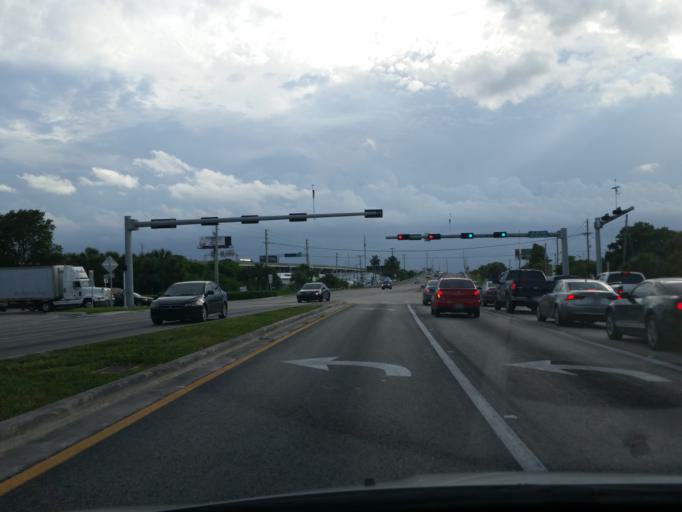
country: US
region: Florida
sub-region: Broward County
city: Melrose Park
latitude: 26.0858
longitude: -80.1798
